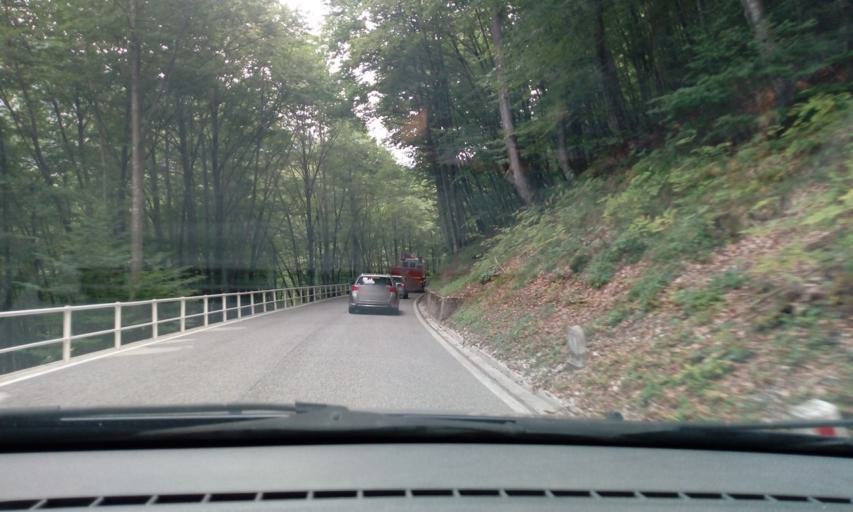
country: IT
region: Friuli Venezia Giulia
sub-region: Provincia di Udine
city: Malborghetto
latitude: 46.3938
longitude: 13.4381
